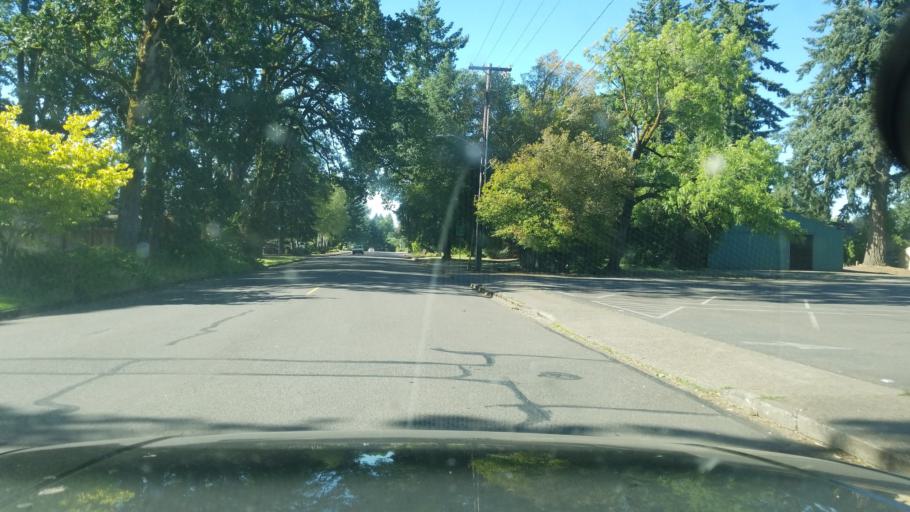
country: US
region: Oregon
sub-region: Yamhill County
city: McMinnville
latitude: 45.2173
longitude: -123.2076
